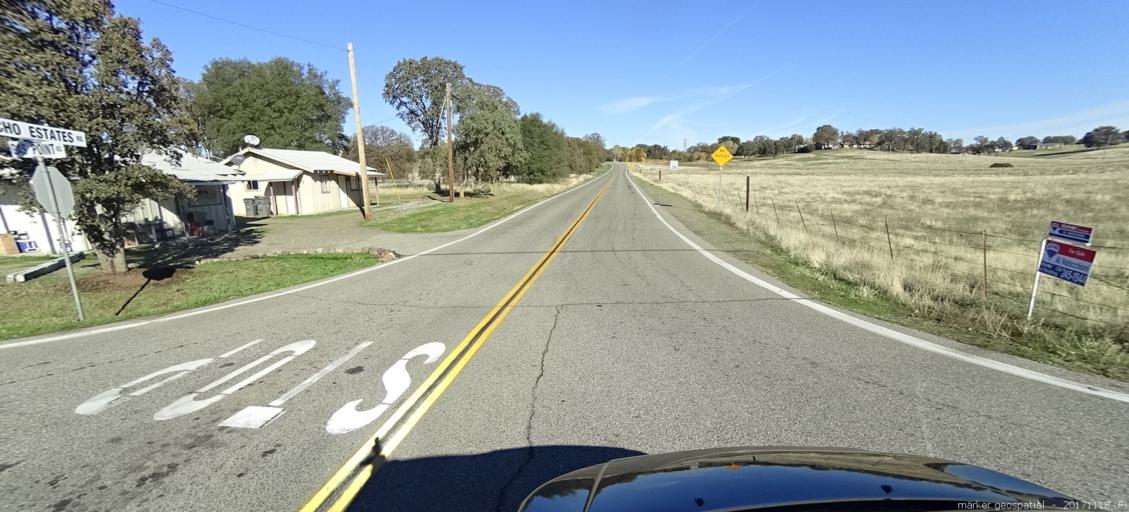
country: US
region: California
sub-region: Shasta County
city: Cottonwood
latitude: 40.3893
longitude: -122.3120
